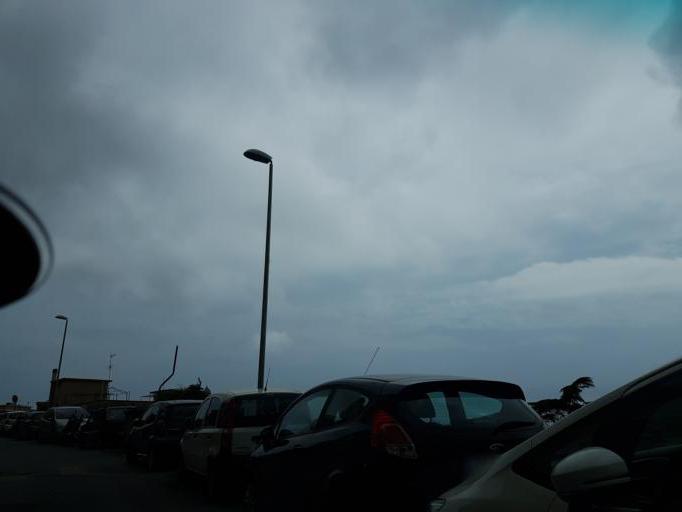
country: IT
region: Liguria
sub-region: Provincia di Genova
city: Genoa
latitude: 44.4236
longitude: 8.9301
